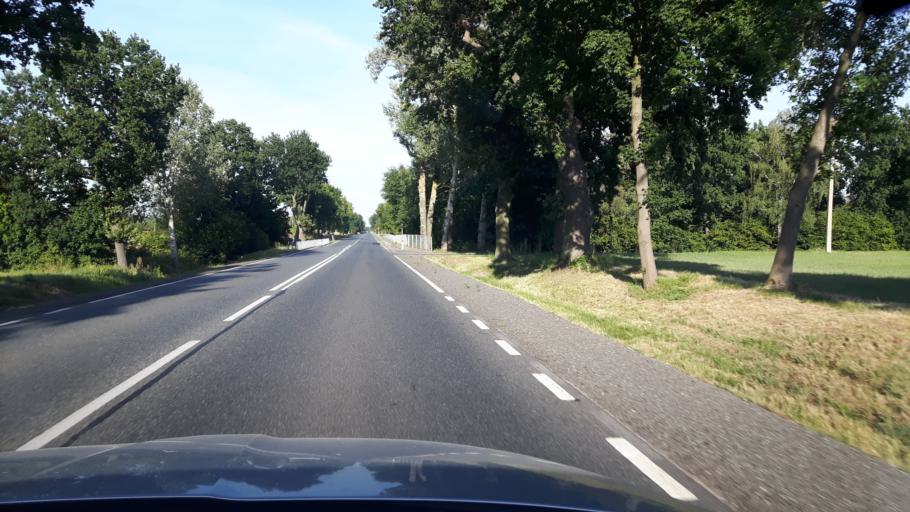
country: PL
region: Masovian Voivodeship
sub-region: Powiat nowodworski
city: Brody-Parcele
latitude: 52.4881
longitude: 20.8130
